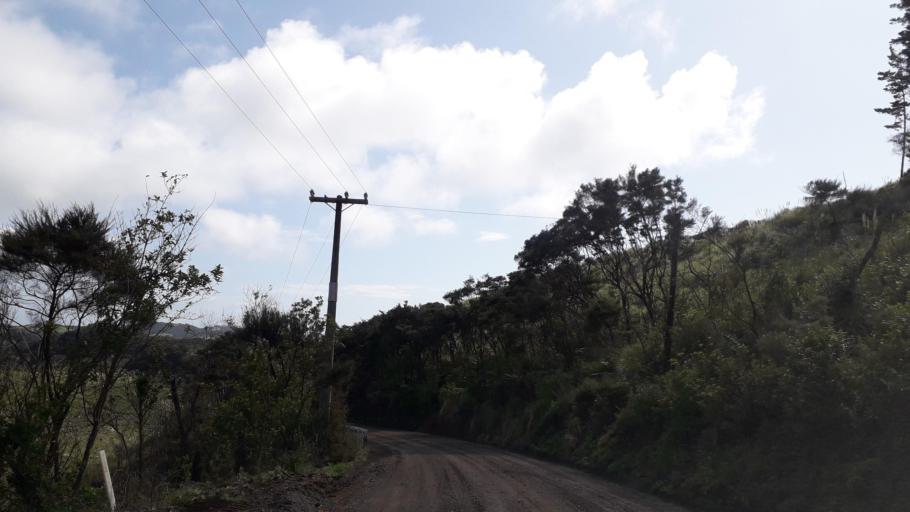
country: NZ
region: Northland
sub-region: Far North District
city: Paihia
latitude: -35.2433
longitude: 174.2483
